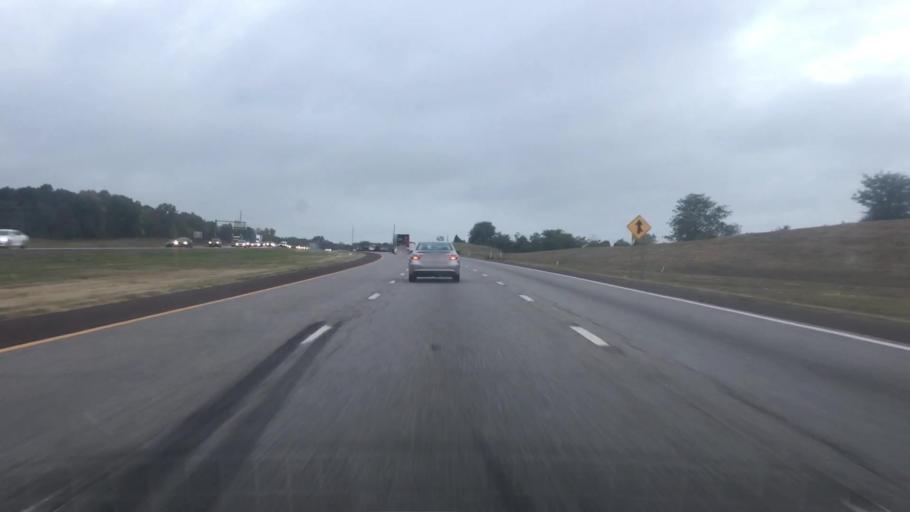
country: US
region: Kansas
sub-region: Wyandotte County
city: Edwardsville
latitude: 39.0889
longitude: -94.8026
